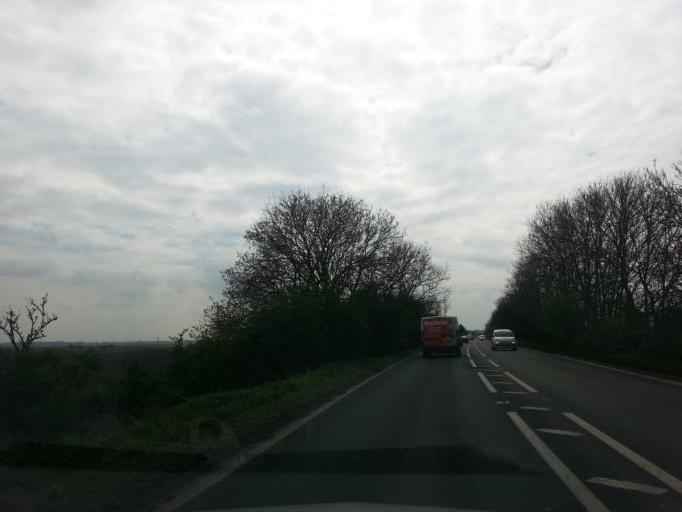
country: GB
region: England
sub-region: Cambridgeshire
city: March
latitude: 52.6188
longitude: 0.0807
